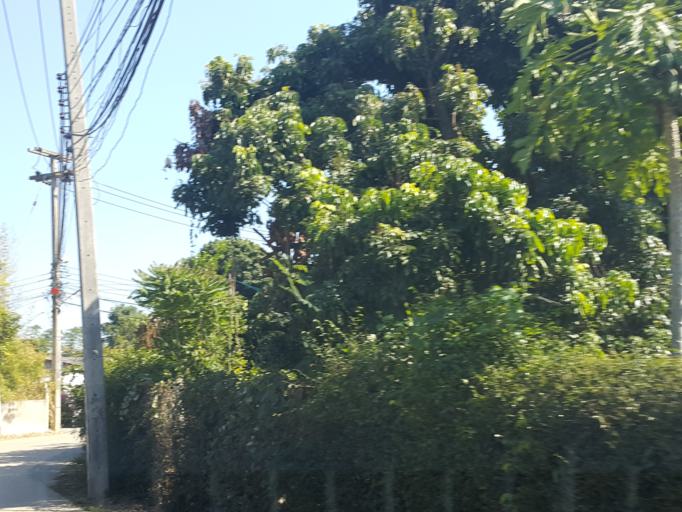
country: TH
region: Chiang Mai
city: San Sai
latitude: 18.8825
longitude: 98.9952
